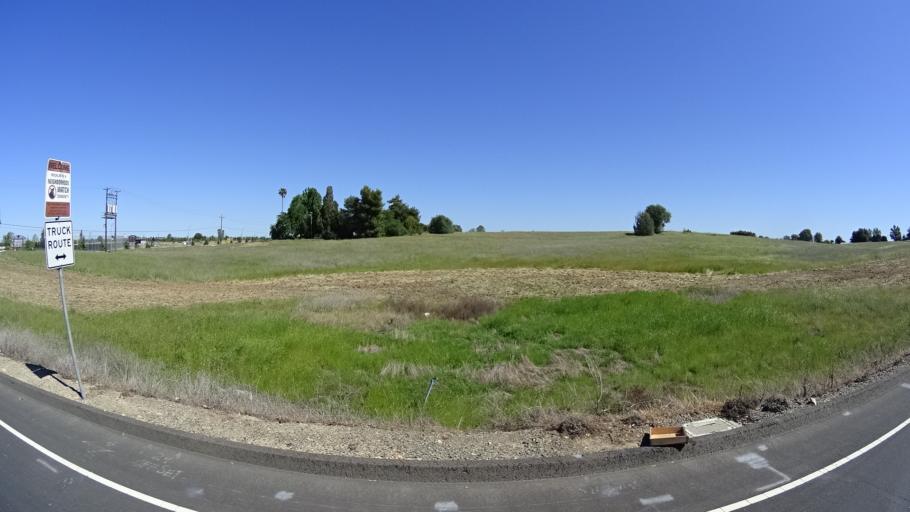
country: US
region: California
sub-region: Placer County
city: Rocklin
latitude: 38.7886
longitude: -121.2048
